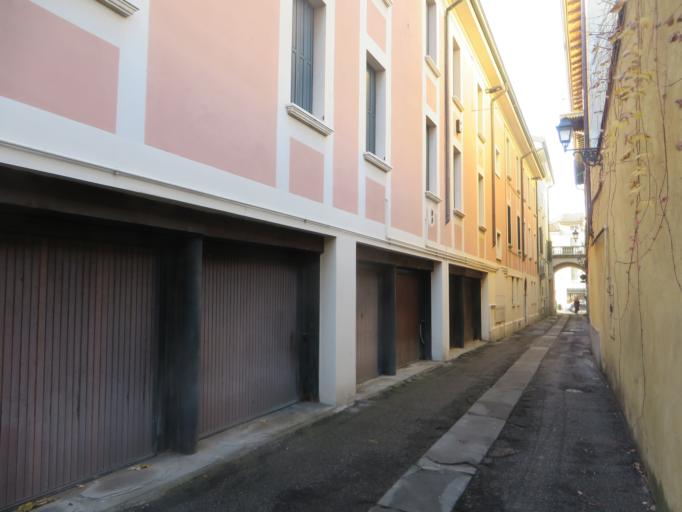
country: IT
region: Lombardy
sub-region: Provincia di Brescia
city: Brescia
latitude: 45.5333
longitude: 10.2239
